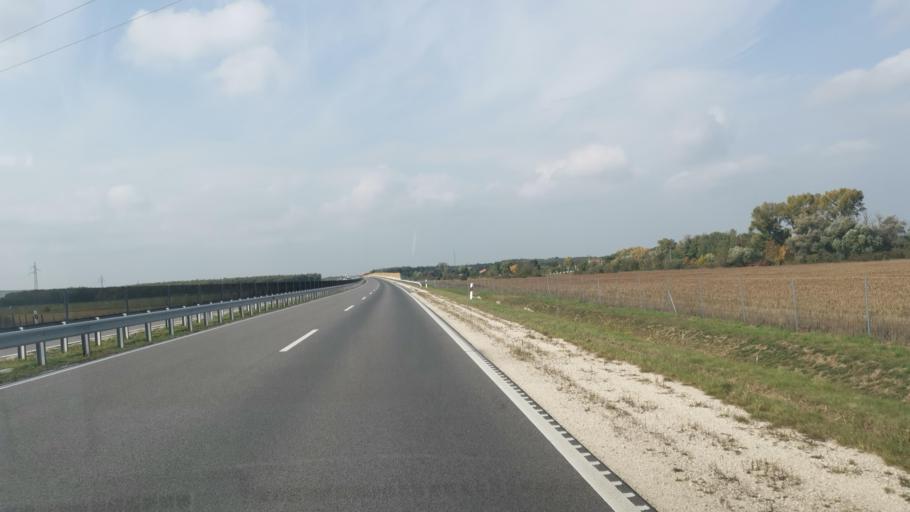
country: HU
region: Gyor-Moson-Sopron
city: Kapuvar
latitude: 47.5805
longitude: 16.9859
